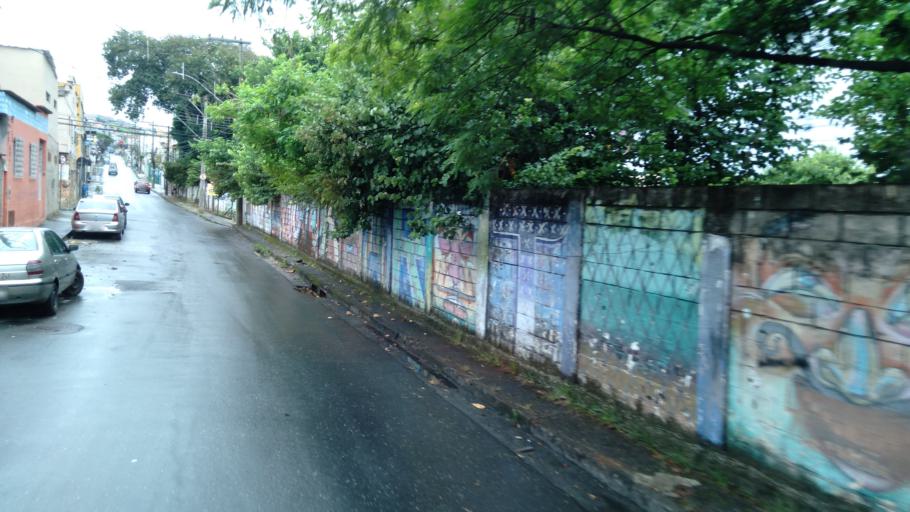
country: BR
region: Minas Gerais
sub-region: Belo Horizonte
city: Belo Horizonte
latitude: -19.9141
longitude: -43.9054
